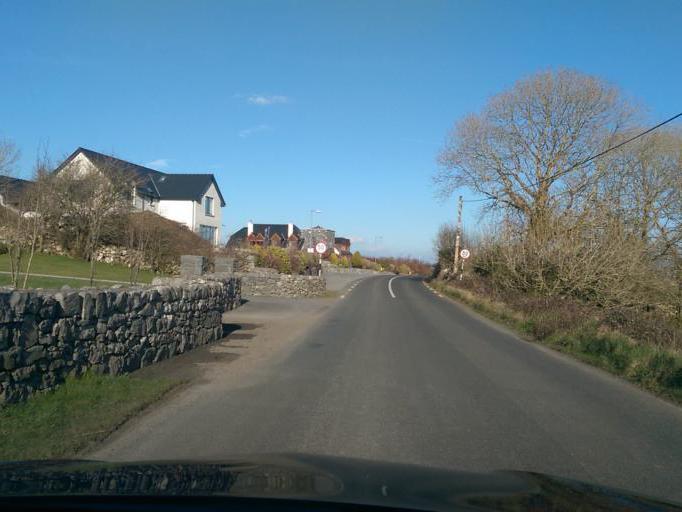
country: IE
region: Connaught
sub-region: County Galway
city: Oranmore
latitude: 53.2286
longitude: -8.8909
